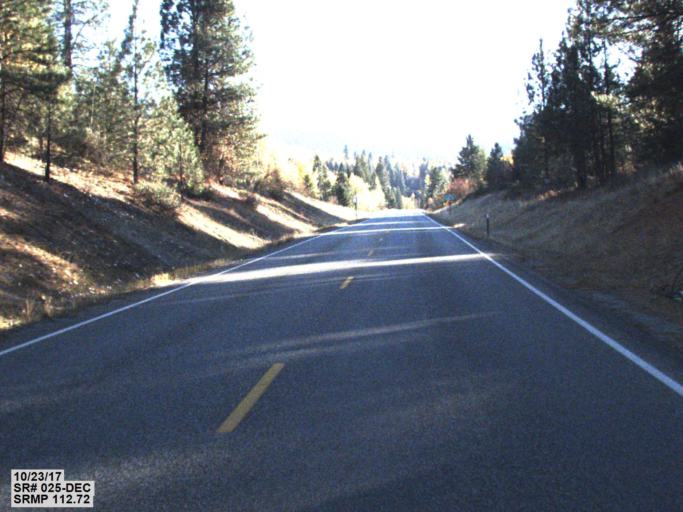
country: CA
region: British Columbia
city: Rossland
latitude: 48.9080
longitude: -117.7922
